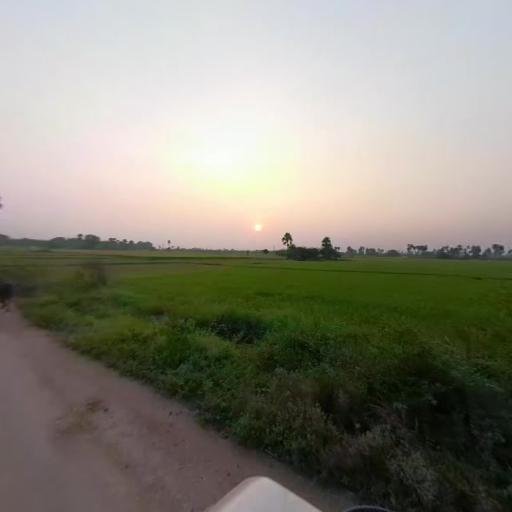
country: IN
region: Telangana
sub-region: Nalgonda
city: Suriapet
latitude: 17.0607
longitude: 79.5473
